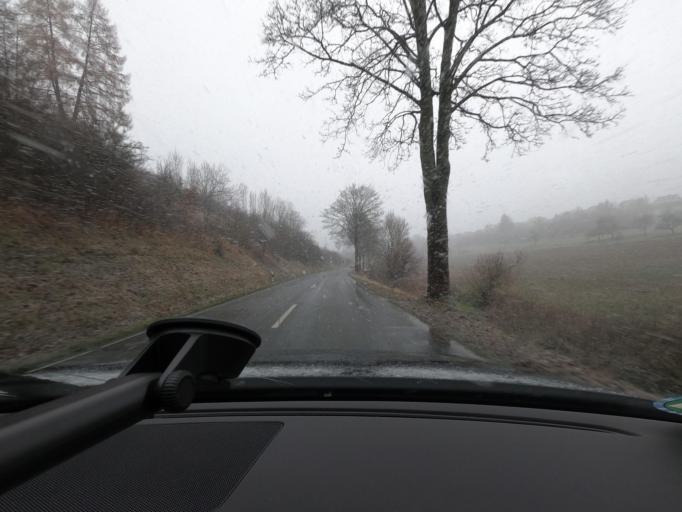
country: DE
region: North Rhine-Westphalia
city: Marsberg
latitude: 51.5040
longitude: 8.9039
